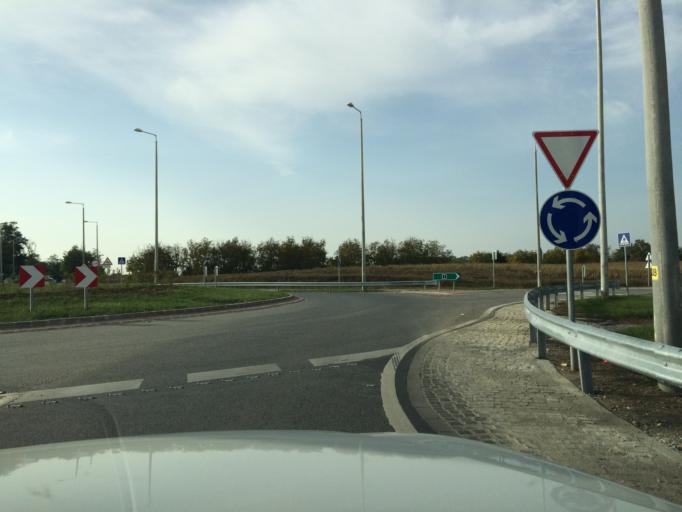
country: HU
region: Szabolcs-Szatmar-Bereg
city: Nyirtelek
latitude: 47.9570
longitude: 21.6527
